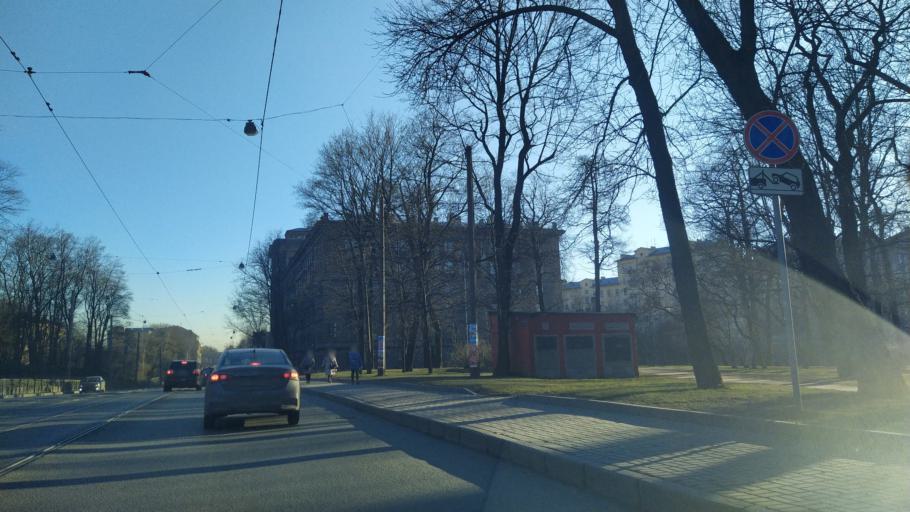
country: RU
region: Leningrad
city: Svetlanovskiy
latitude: 59.9970
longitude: 30.3301
